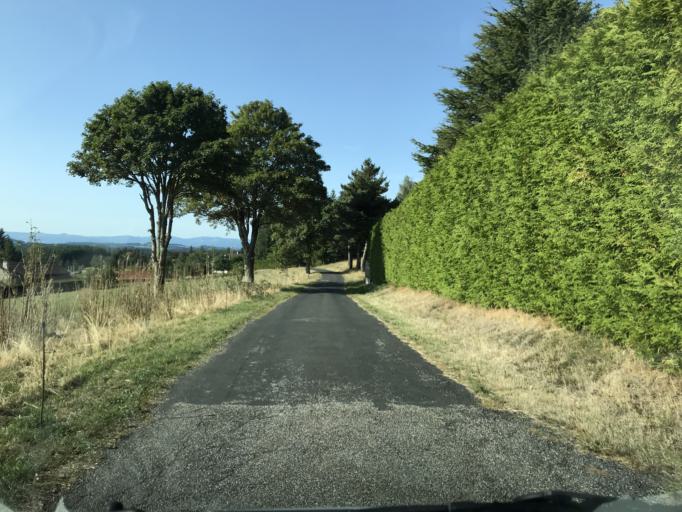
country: FR
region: Rhone-Alpes
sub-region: Departement de l'Ardeche
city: Saint-Agreve
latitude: 45.0296
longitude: 4.4437
